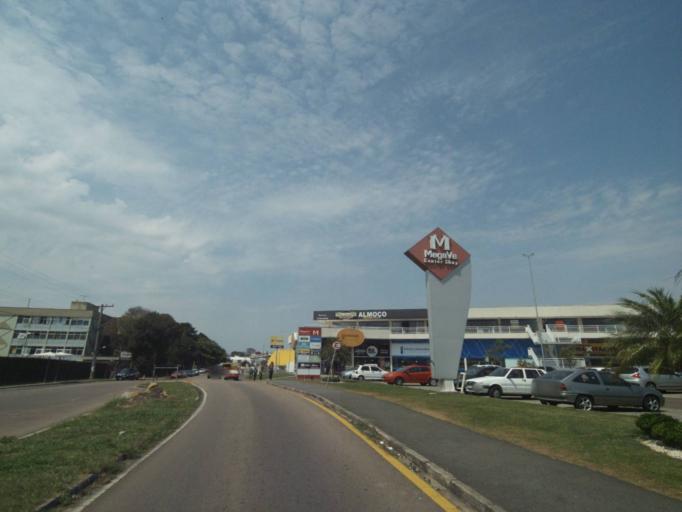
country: BR
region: Parana
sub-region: Curitiba
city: Curitiba
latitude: -25.4761
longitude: -49.3265
